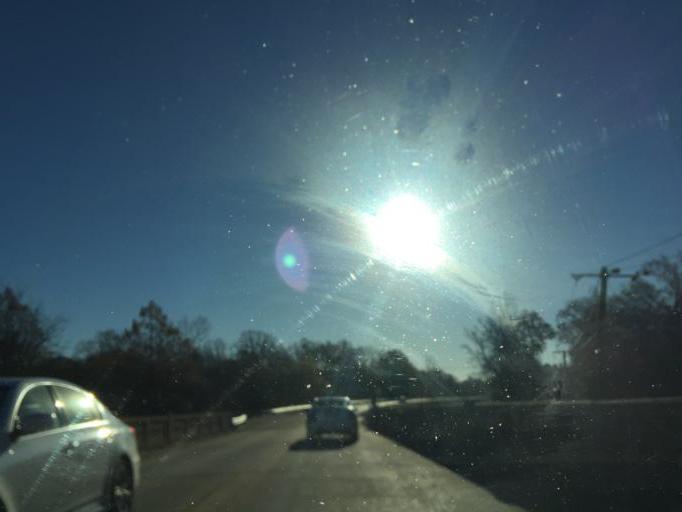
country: US
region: Mississippi
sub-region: Hinds County
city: Jackson
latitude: 32.2884
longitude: -90.1770
